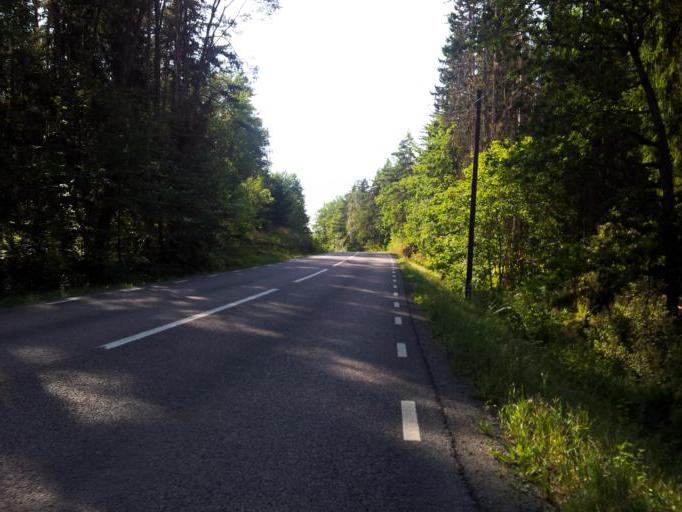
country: SE
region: Uppsala
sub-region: Knivsta Kommun
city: Knivsta
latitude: 59.8774
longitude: 18.0160
